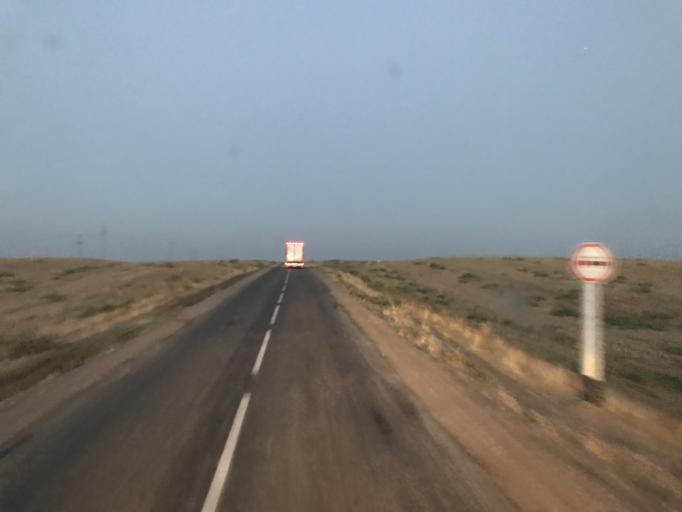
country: UZ
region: Toshkent
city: Chinoz
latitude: 41.1443
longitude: 68.6950
